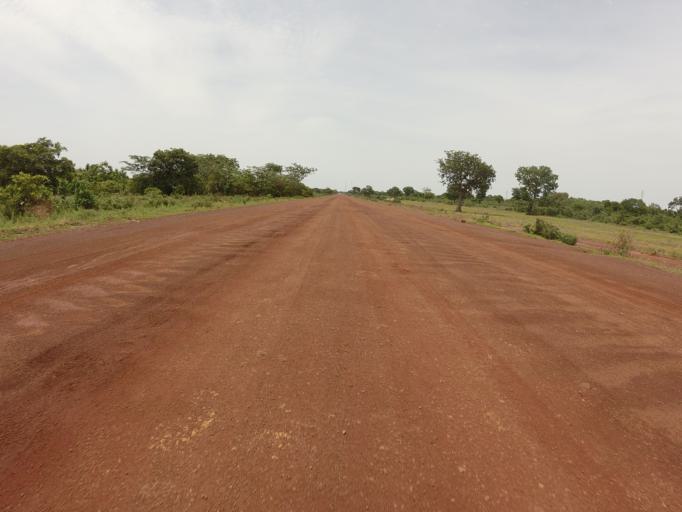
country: GH
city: Kpandae
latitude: 8.8867
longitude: 0.0280
